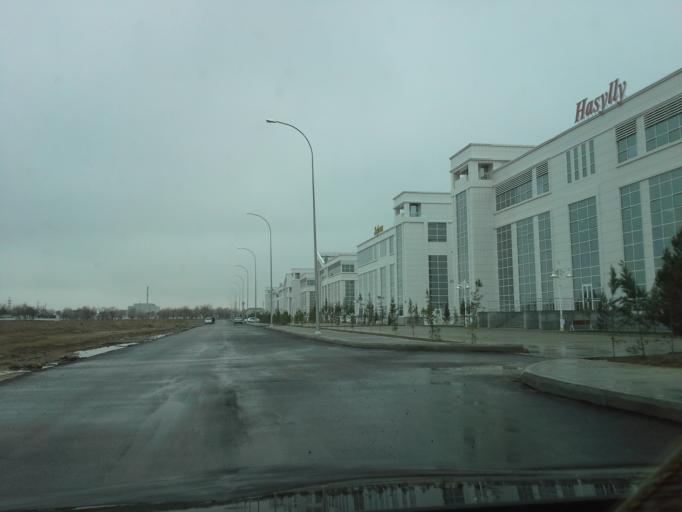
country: TM
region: Ahal
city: Ashgabat
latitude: 37.9510
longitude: 58.4303
